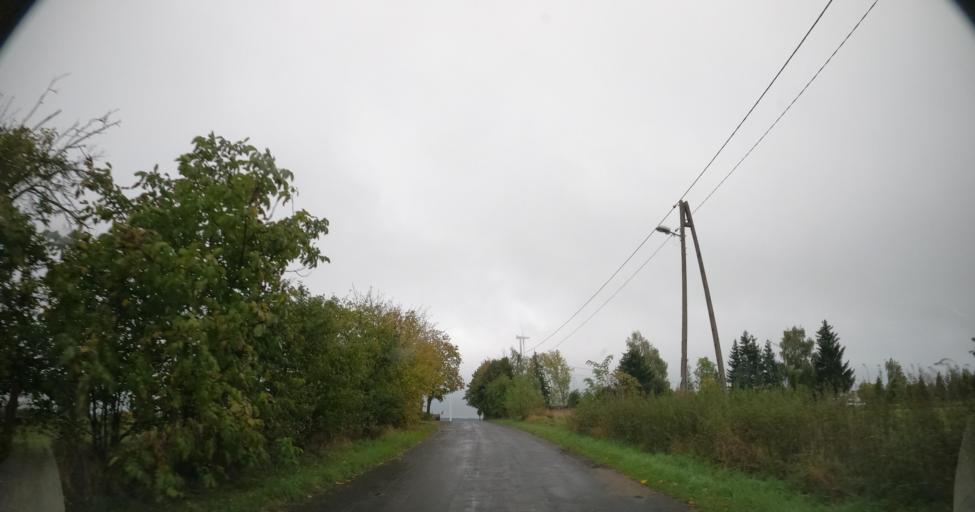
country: PL
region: West Pomeranian Voivodeship
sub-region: Powiat pyrzycki
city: Kozielice
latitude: 53.0898
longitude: 14.7722
